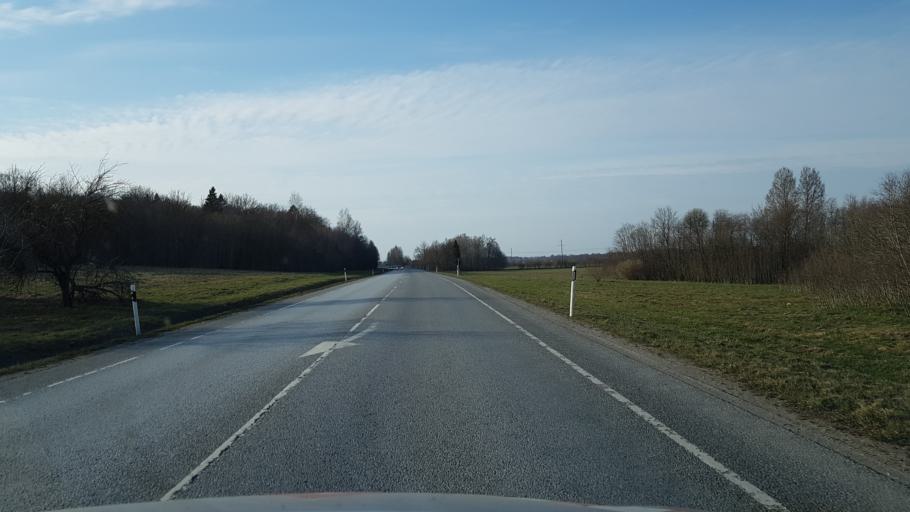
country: EE
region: Laeaene-Virumaa
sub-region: Haljala vald
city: Haljala
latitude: 59.3969
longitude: 26.3082
